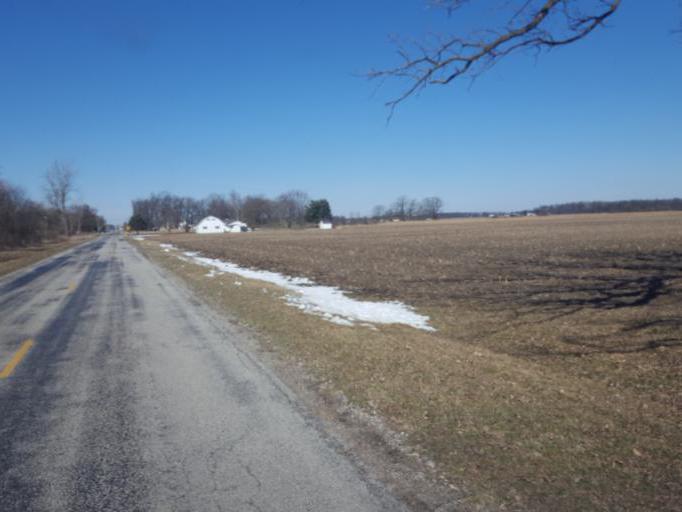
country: US
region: Ohio
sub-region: Marion County
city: Marion
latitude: 40.6521
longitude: -83.0763
